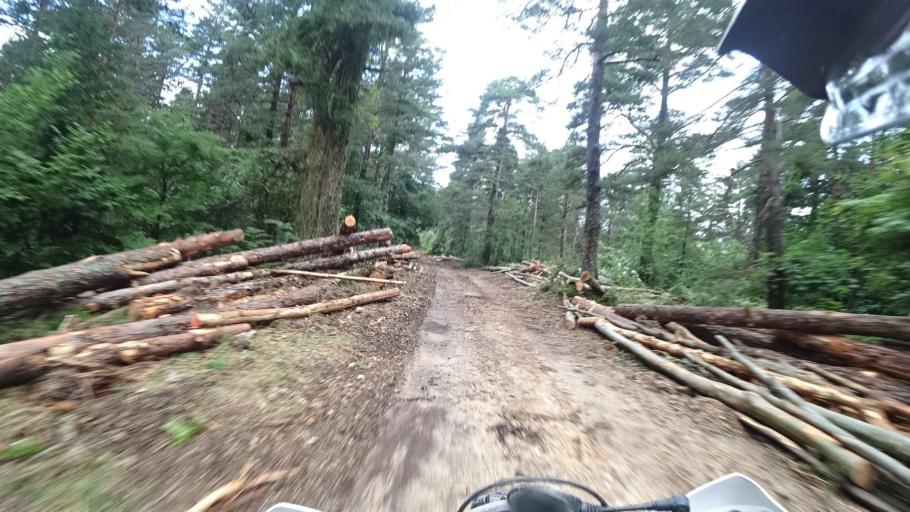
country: HR
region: Licko-Senjska
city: Otocac
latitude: 44.8712
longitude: 15.3997
